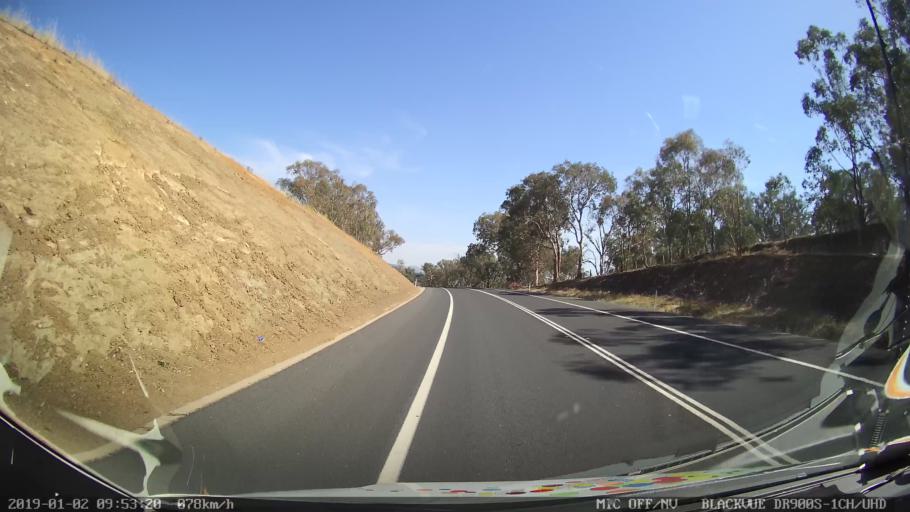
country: AU
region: New South Wales
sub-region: Tumut Shire
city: Tumut
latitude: -35.2491
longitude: 148.2033
